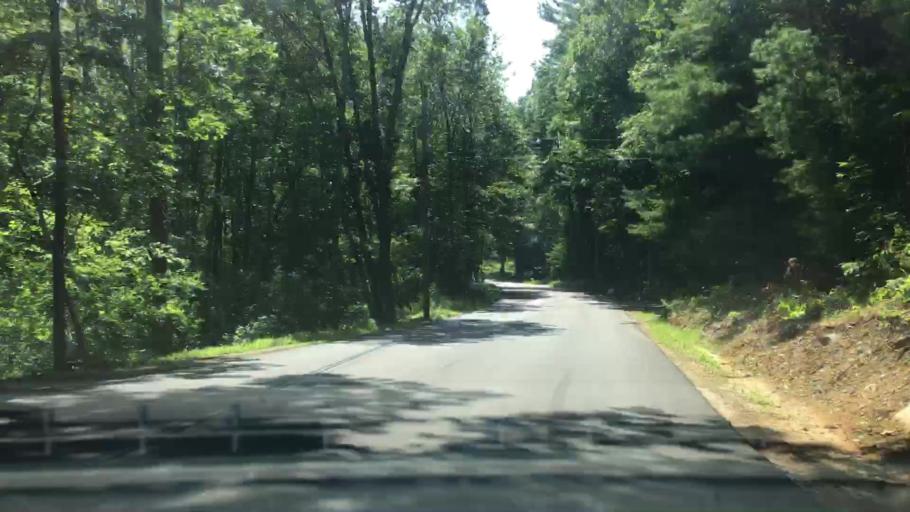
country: US
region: New Hampshire
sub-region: Rockingham County
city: Hampstead
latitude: 42.8829
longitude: -71.2208
